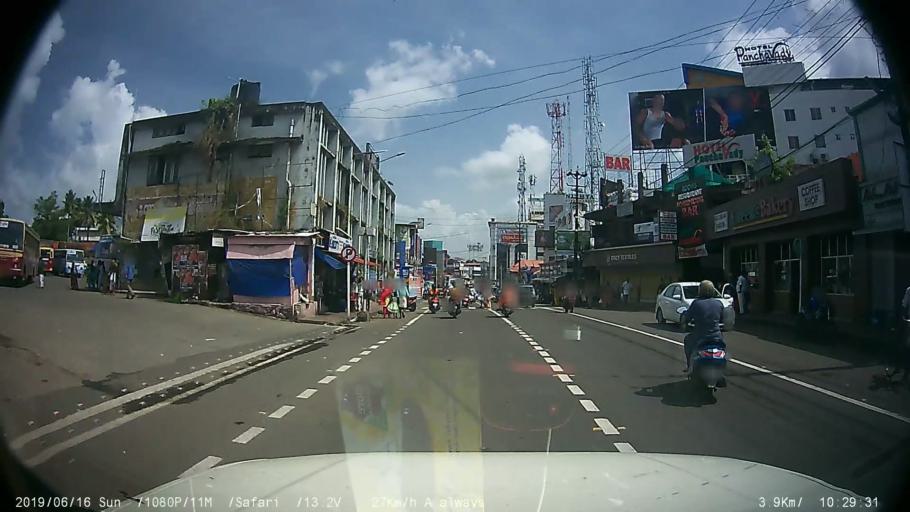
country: IN
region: Kerala
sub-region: Kottayam
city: Changanacheri
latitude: 9.4455
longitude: 76.5413
